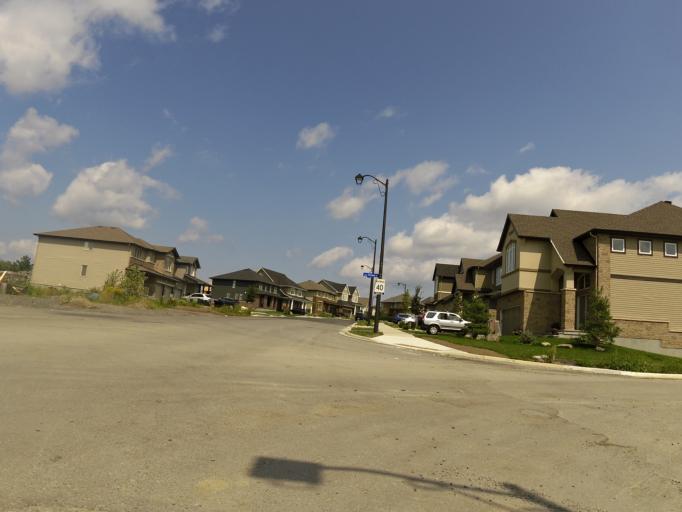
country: CA
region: Ontario
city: Bells Corners
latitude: 45.3184
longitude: -75.9435
